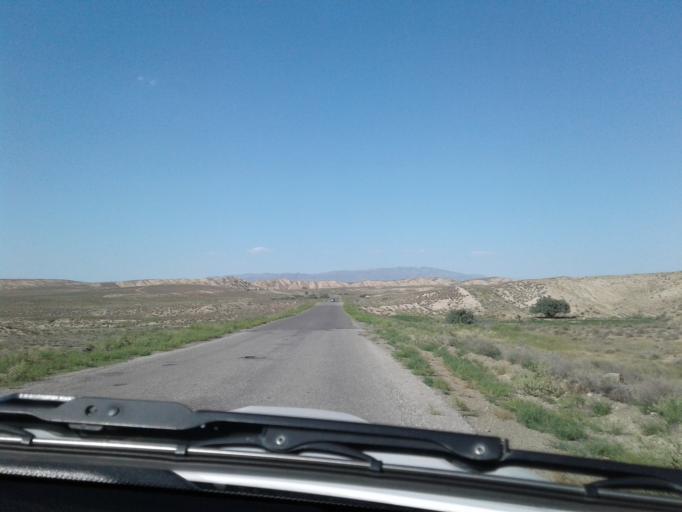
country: TM
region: Balkan
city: Magtymguly
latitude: 38.6406
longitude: 56.2537
